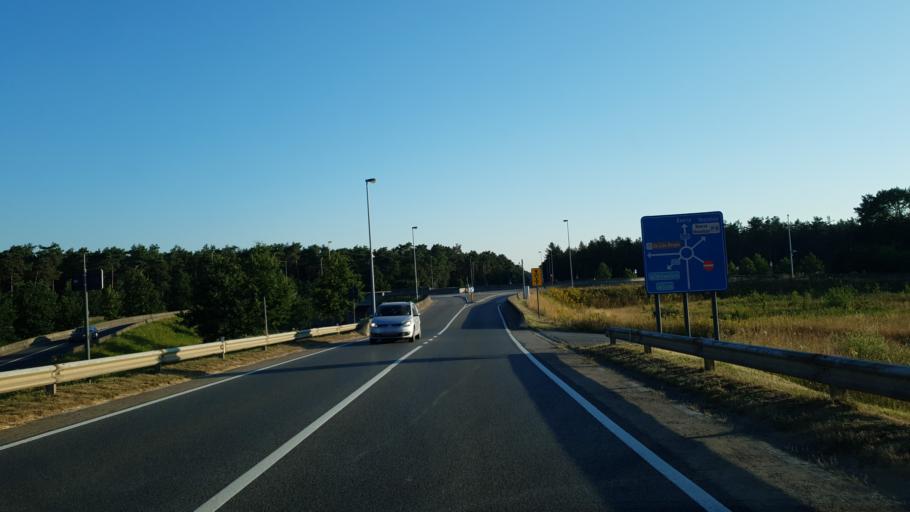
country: BE
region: Flanders
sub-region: Provincie Antwerpen
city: Beerse
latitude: 51.2873
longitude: 4.8552
